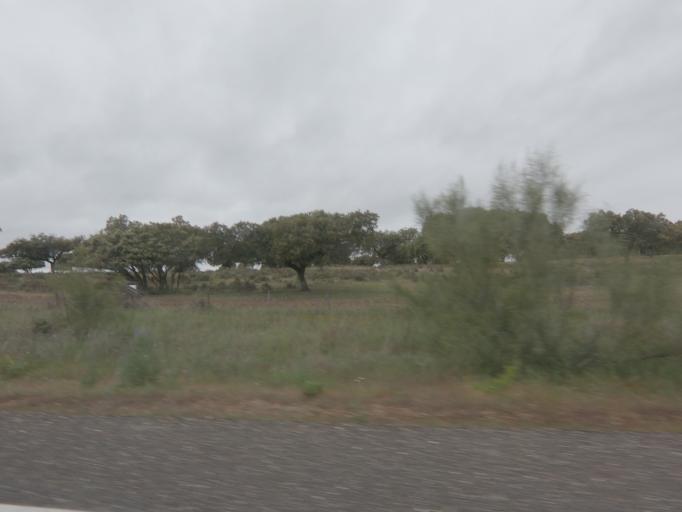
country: ES
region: Extremadura
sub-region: Provincia de Badajoz
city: La Roca de la Sierra
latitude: 39.0724
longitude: -6.7538
